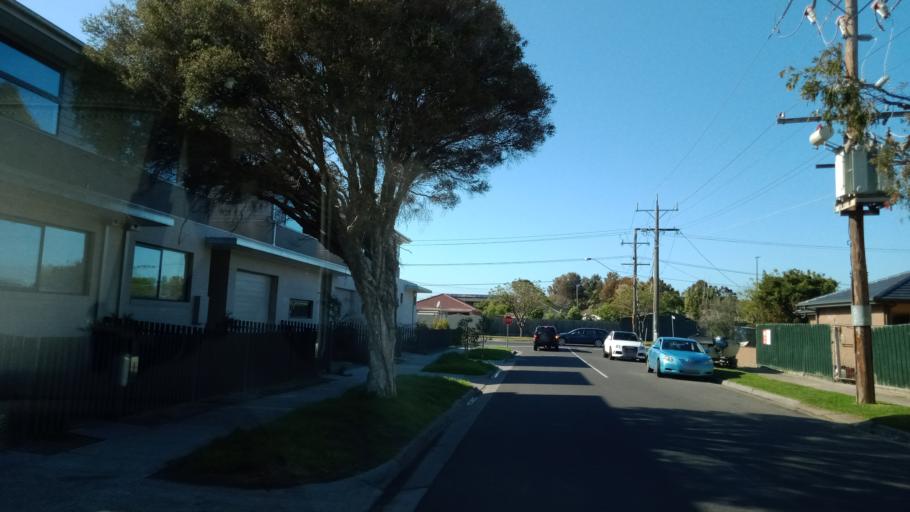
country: AU
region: Victoria
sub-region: Kingston
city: Chelsea Heights
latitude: -38.0461
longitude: 145.1324
